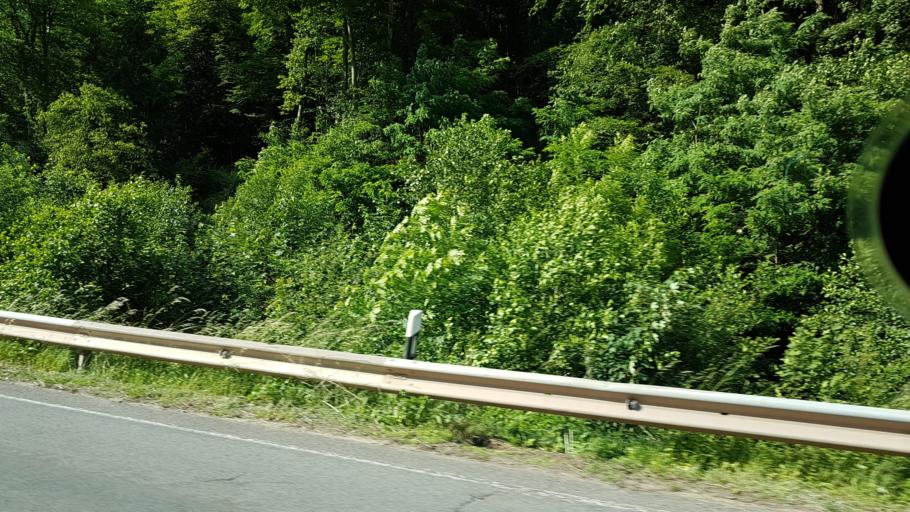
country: DE
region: Rheinland-Pfalz
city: Dennweiler-Frohnbach
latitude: 49.6161
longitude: 7.3742
